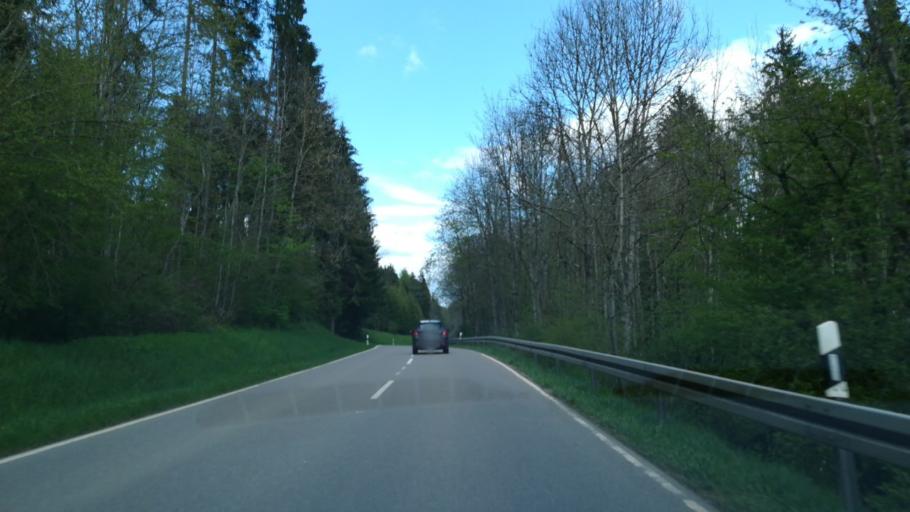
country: DE
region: Baden-Wuerttemberg
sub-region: Freiburg Region
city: Bonndorf im Schwarzwald
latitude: 47.8289
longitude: 8.4177
